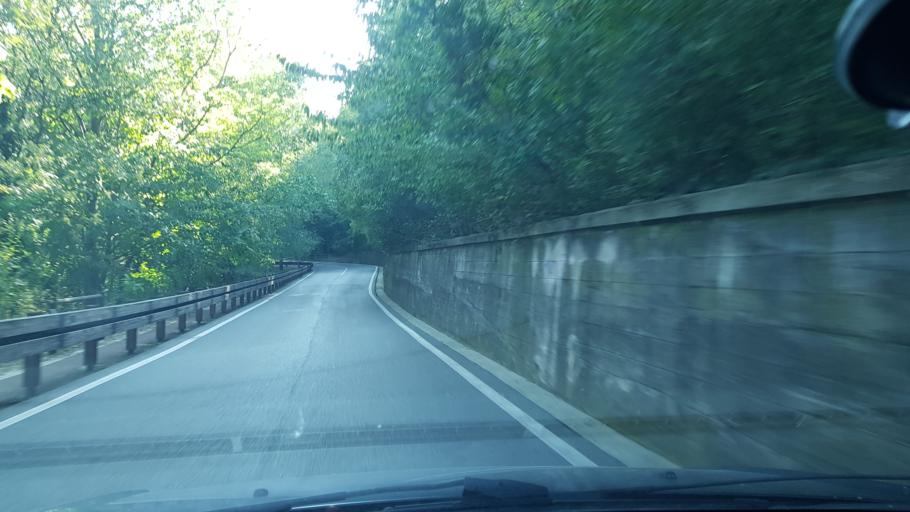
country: IT
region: Friuli Venezia Giulia
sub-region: Provincia di Trieste
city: Trieste
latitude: 45.6487
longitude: 13.8085
